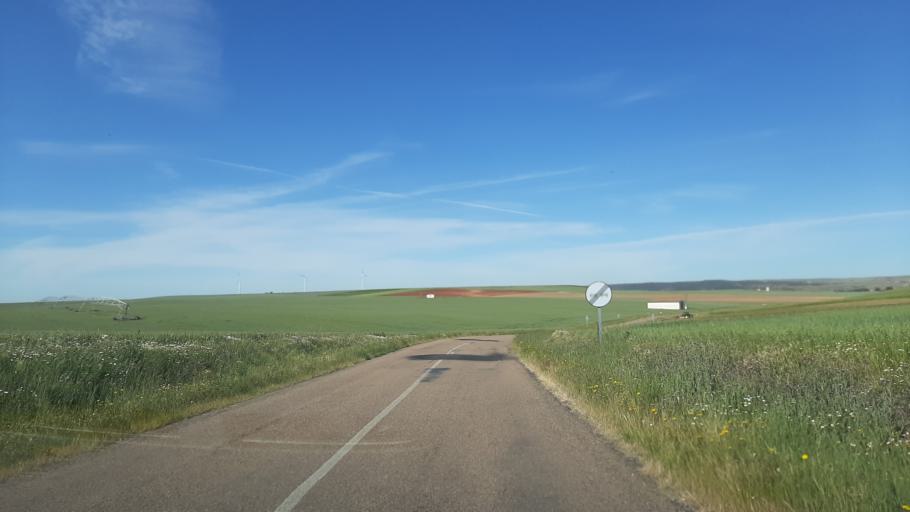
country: ES
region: Castille and Leon
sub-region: Provincia de Salamanca
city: Aldeaseca de Alba
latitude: 40.8175
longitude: -5.4603
